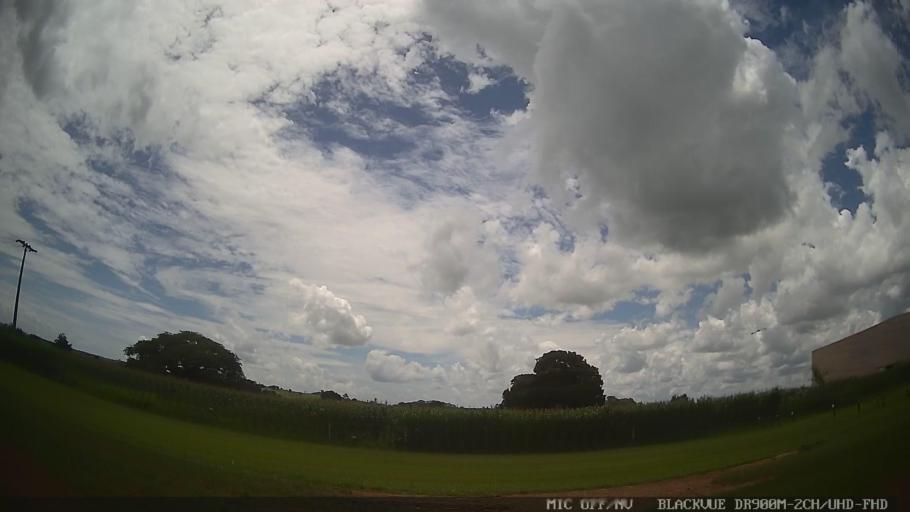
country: BR
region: Sao Paulo
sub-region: Laranjal Paulista
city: Laranjal Paulista
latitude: -23.0426
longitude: -47.9088
